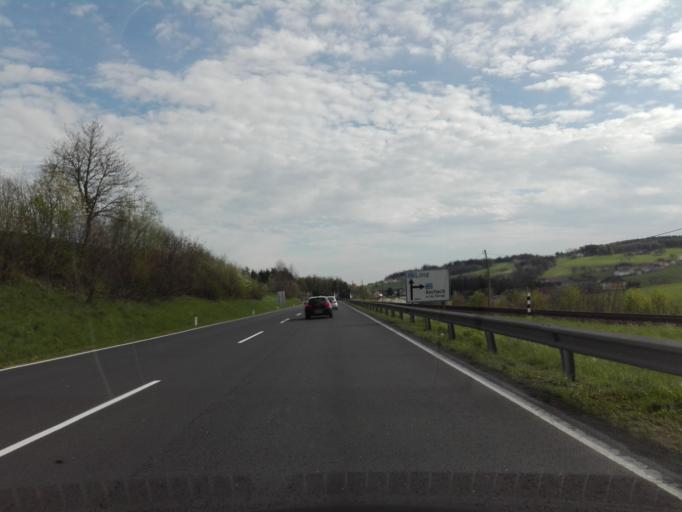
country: AT
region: Upper Austria
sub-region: Politischer Bezirk Urfahr-Umgebung
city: Sankt Gotthard im Muhlkreis
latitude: 48.3906
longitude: 14.0891
